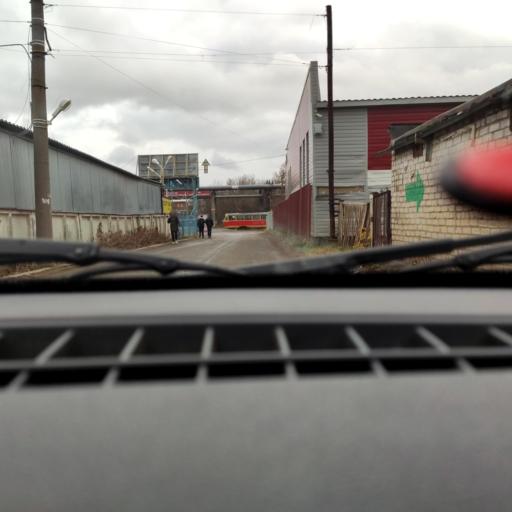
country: RU
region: Bashkortostan
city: Ufa
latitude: 54.7997
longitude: 56.0913
